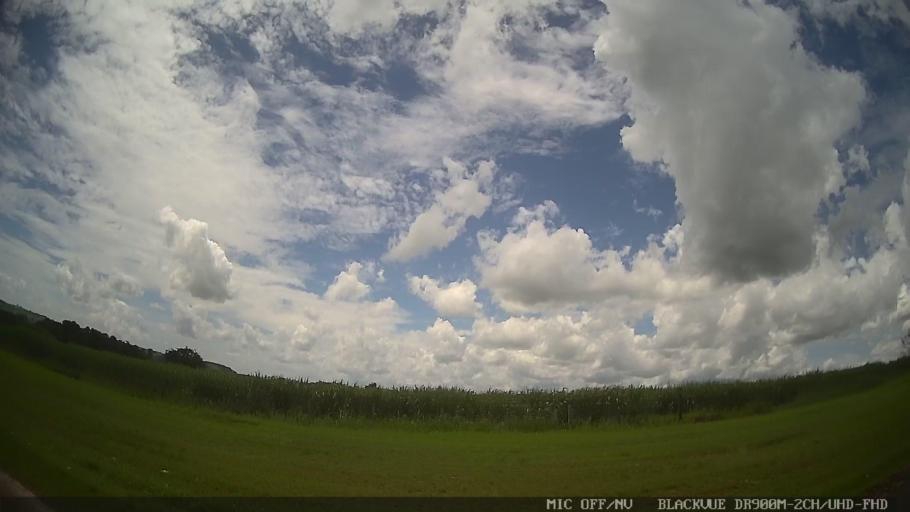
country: BR
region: Sao Paulo
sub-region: Laranjal Paulista
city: Laranjal Paulista
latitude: -23.0465
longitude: -47.9232
